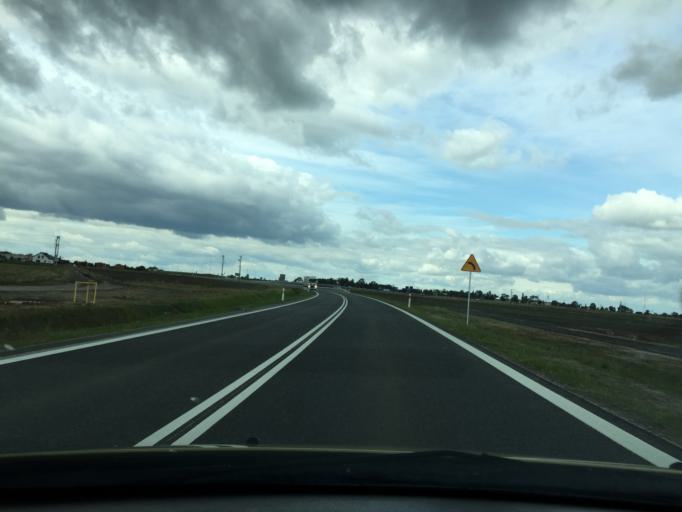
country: PL
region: Greater Poland Voivodeship
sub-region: Powiat jarocinski
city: Jarocin
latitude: 51.9734
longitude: 17.5266
